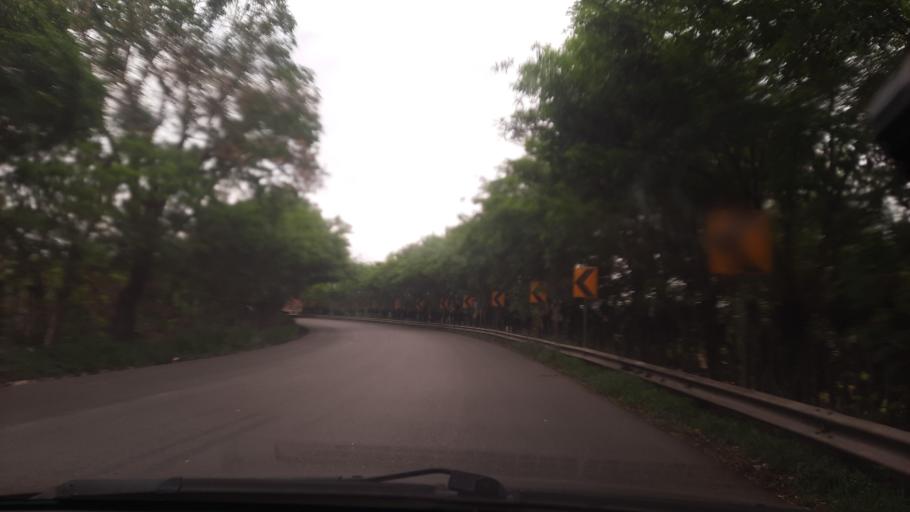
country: GT
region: Izabal
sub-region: Municipio de Los Amates
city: Los Amates
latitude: 15.2528
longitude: -89.1205
